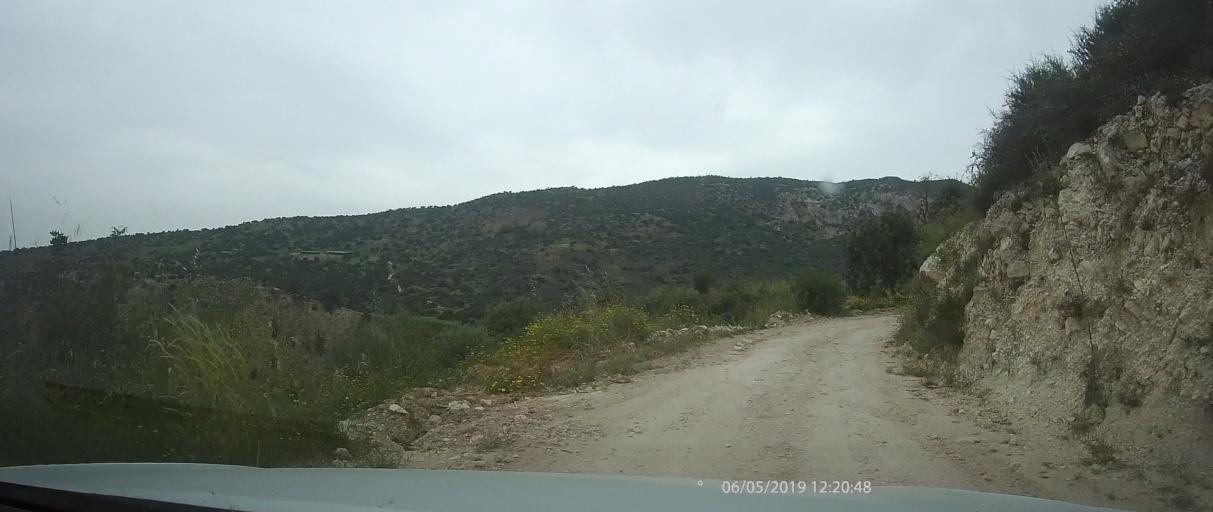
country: CY
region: Pafos
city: Tala
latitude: 34.8629
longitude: 32.4313
